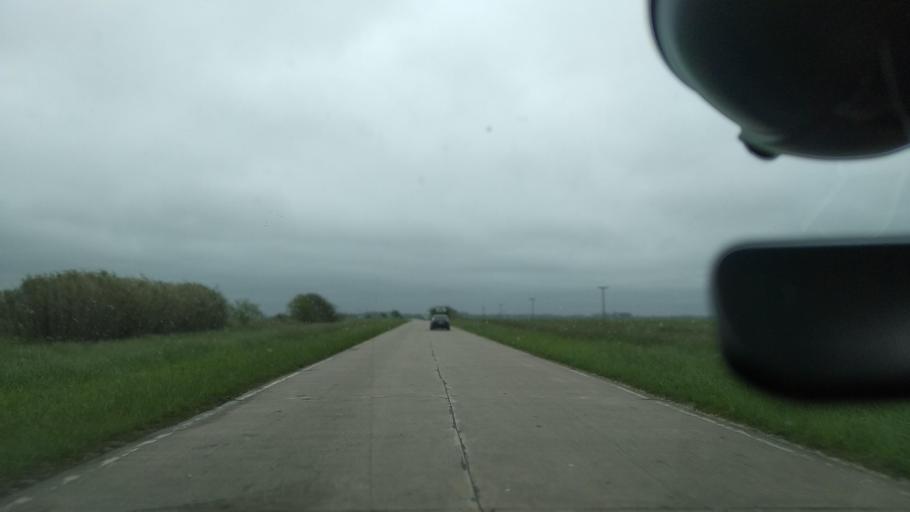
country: AR
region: Buenos Aires
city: Veronica
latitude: -35.5672
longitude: -57.2908
